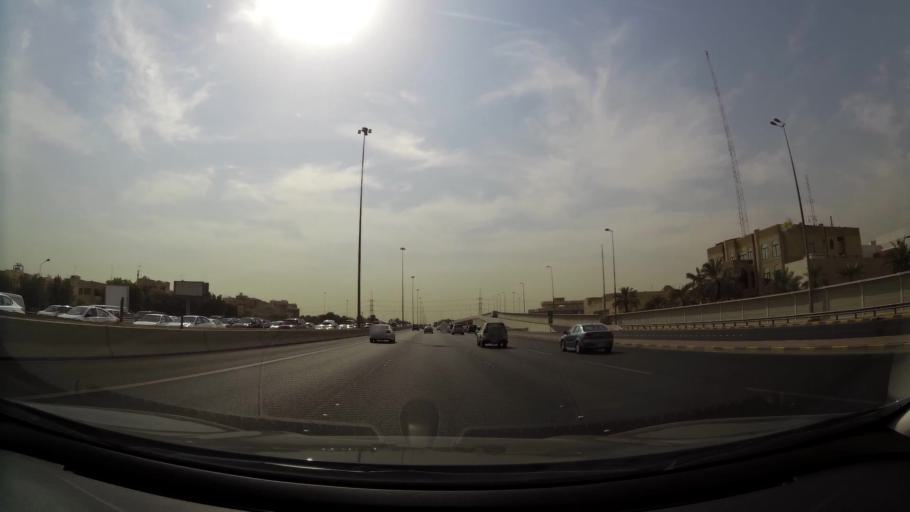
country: KW
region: Al Farwaniyah
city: Al Farwaniyah
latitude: 29.3097
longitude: 47.9772
